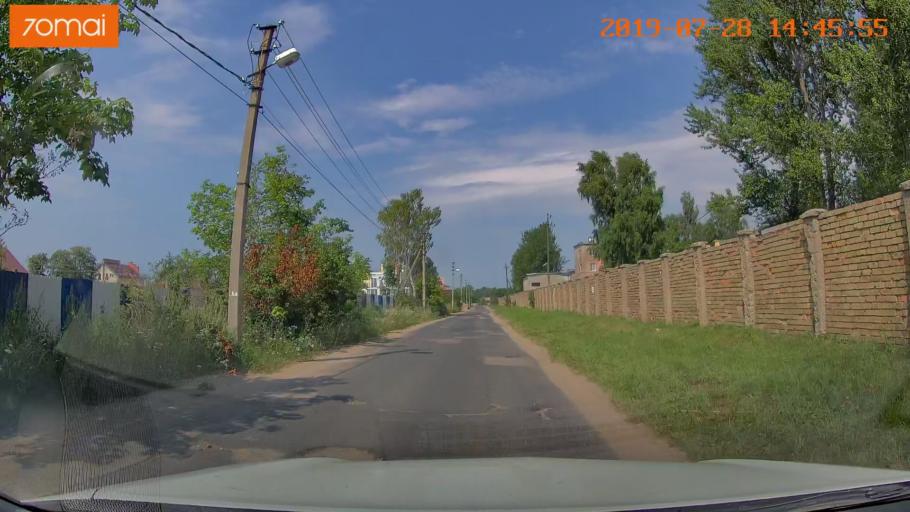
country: RU
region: Kaliningrad
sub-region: Gorod Kaliningrad
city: Yantarnyy
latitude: 54.8735
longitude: 19.9396
